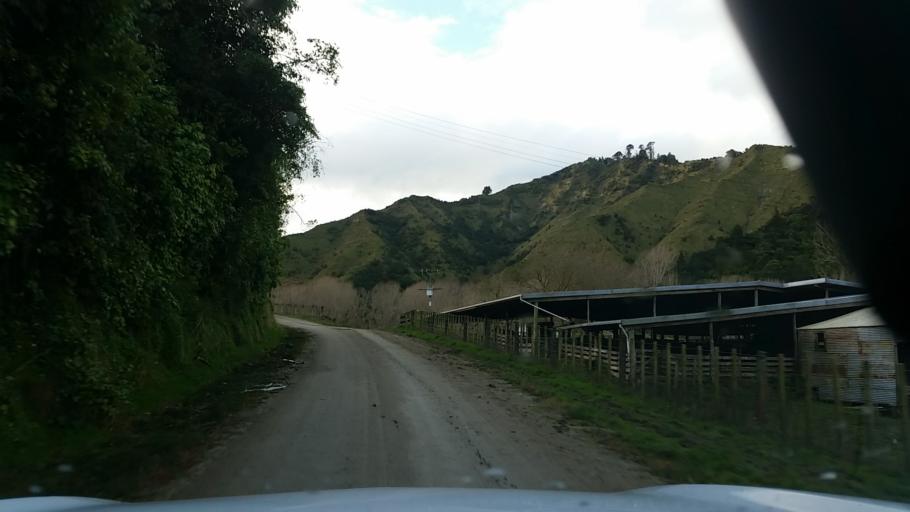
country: NZ
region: Taranaki
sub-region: South Taranaki District
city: Patea
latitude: -39.5607
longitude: 174.8056
